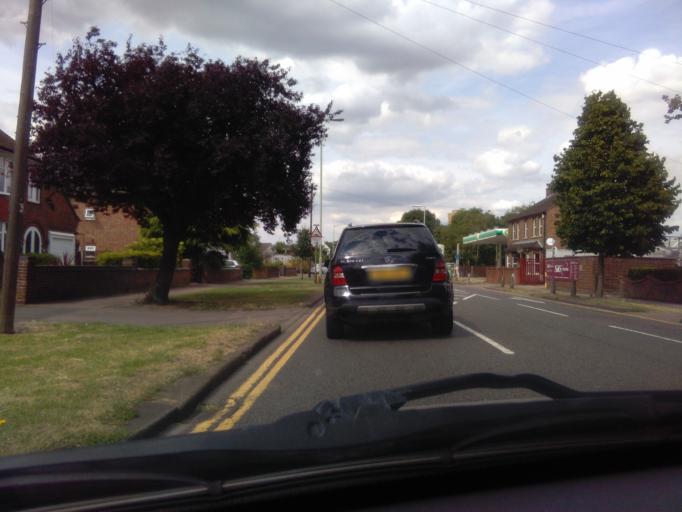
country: GB
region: England
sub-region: Bedford
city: Bedford
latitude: 52.1382
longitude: -0.4442
